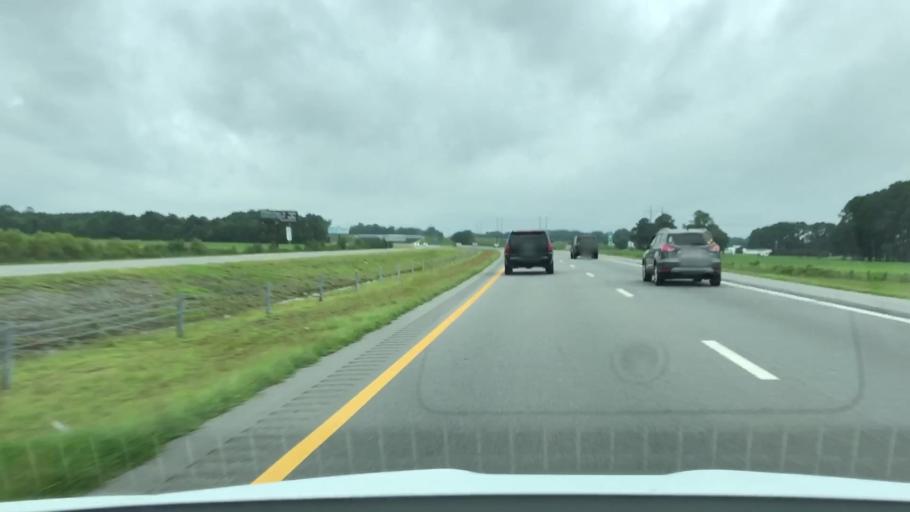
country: US
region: North Carolina
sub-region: Wayne County
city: Elroy
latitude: 35.4172
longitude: -77.9123
